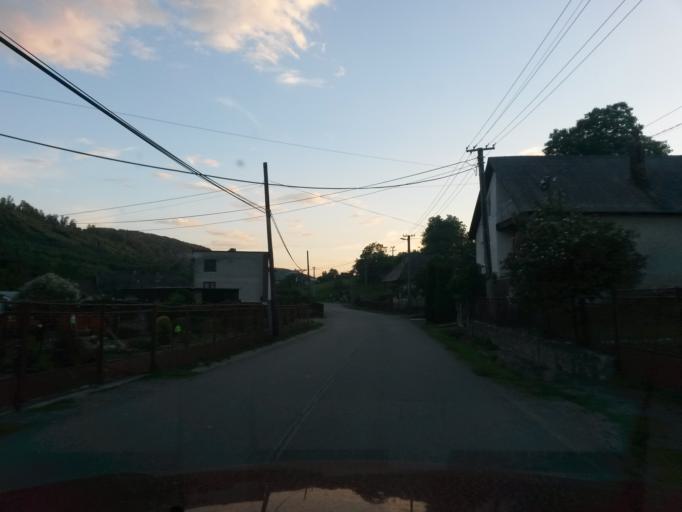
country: UA
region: Zakarpattia
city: Kamianytsia
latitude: 48.8076
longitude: 22.3231
